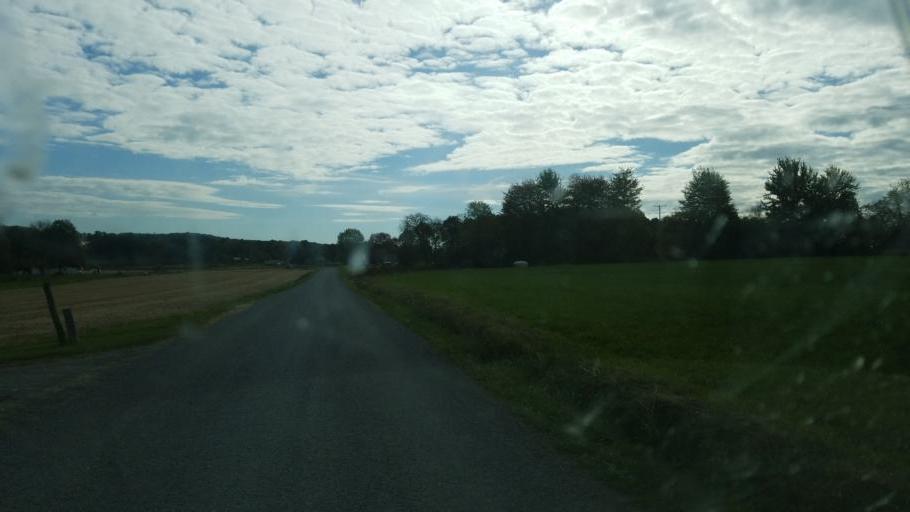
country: US
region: Pennsylvania
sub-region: Mercer County
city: Reynolds Heights
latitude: 41.3352
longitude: -80.3025
